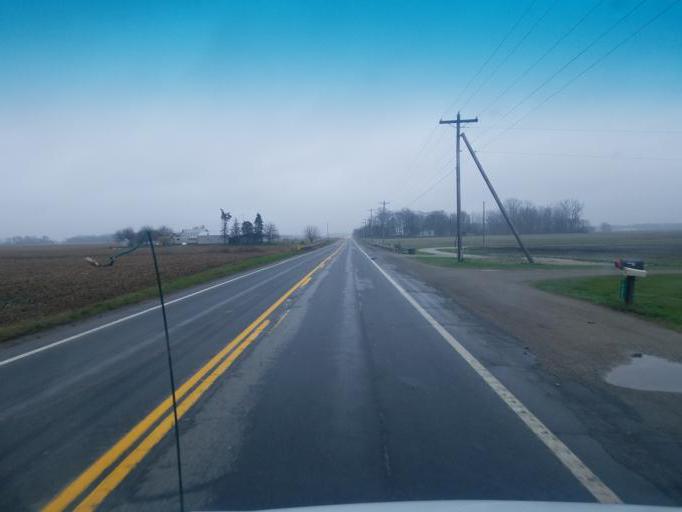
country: US
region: Ohio
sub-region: Wood County
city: Weston
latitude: 41.3722
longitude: -83.7746
